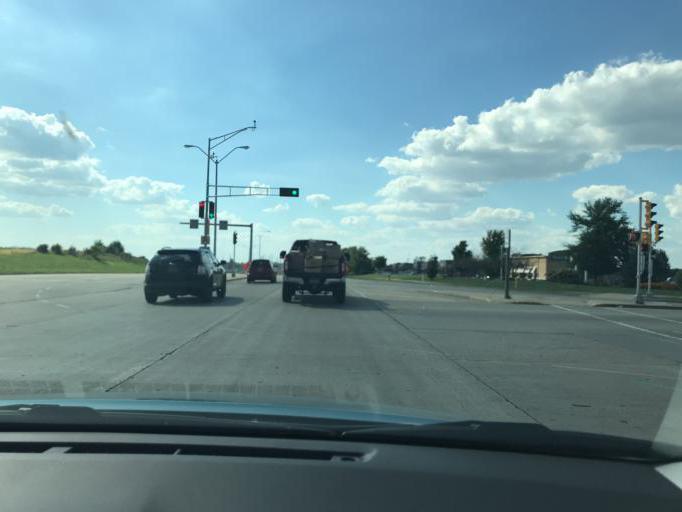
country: US
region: Wisconsin
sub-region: Walworth County
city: Delavan
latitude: 42.6280
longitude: -88.6095
